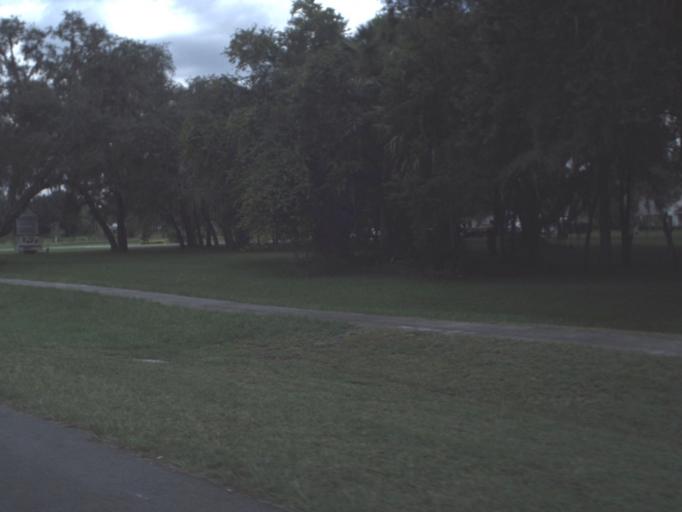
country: US
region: Florida
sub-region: Pasco County
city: Trinity
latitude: 28.1565
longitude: -82.6962
